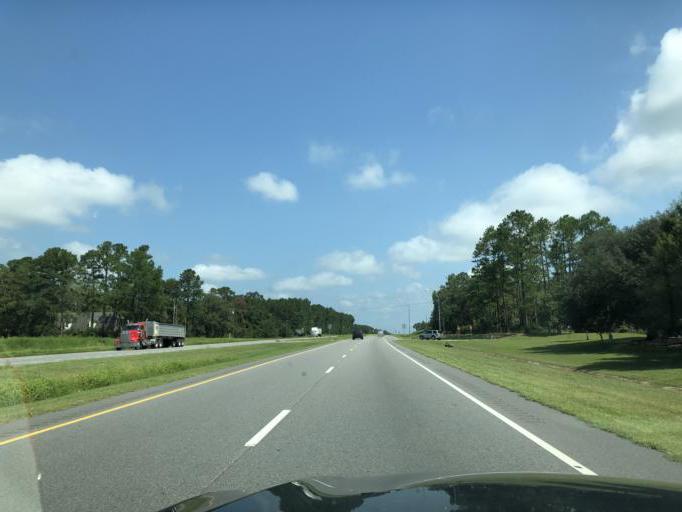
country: US
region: Alabama
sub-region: Houston County
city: Cottonwood
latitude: 31.0088
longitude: -85.4078
